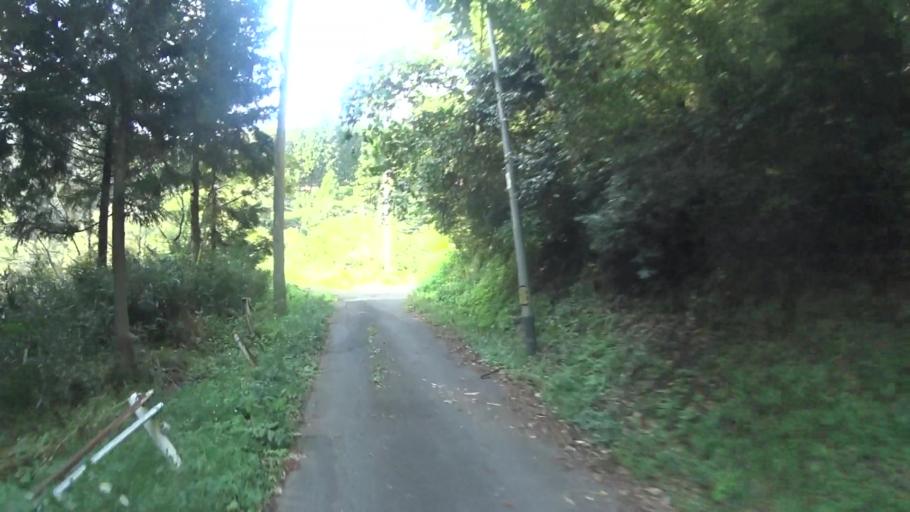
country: JP
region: Kyoto
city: Miyazu
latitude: 35.7205
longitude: 135.1638
